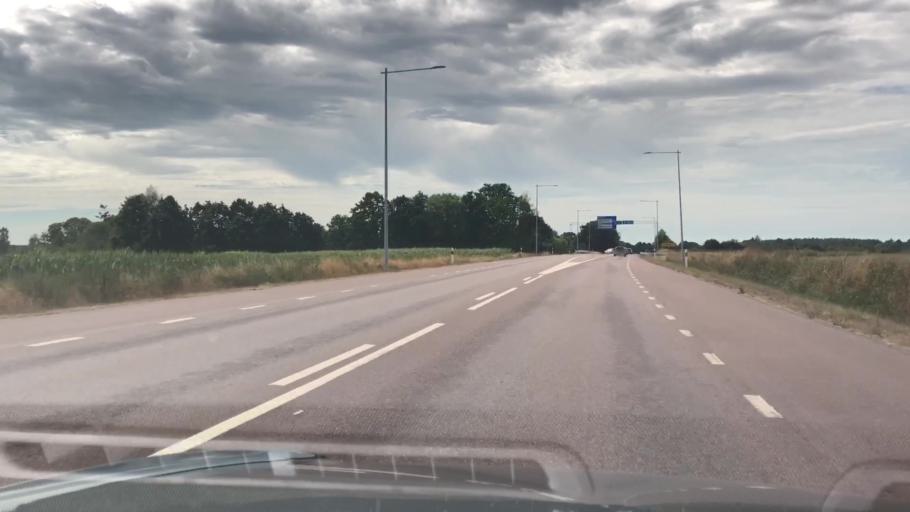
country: SE
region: Kalmar
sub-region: Torsas Kommun
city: Torsas
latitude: 56.3238
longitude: 16.0350
